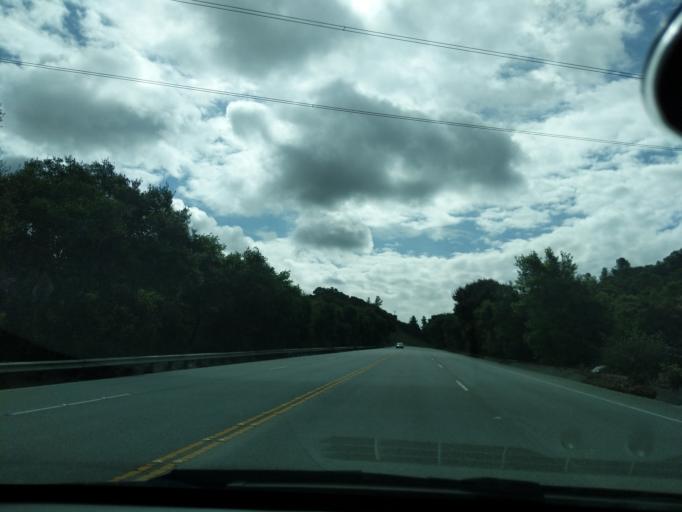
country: US
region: California
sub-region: San Benito County
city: Aromas
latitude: 36.8867
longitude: -121.6652
